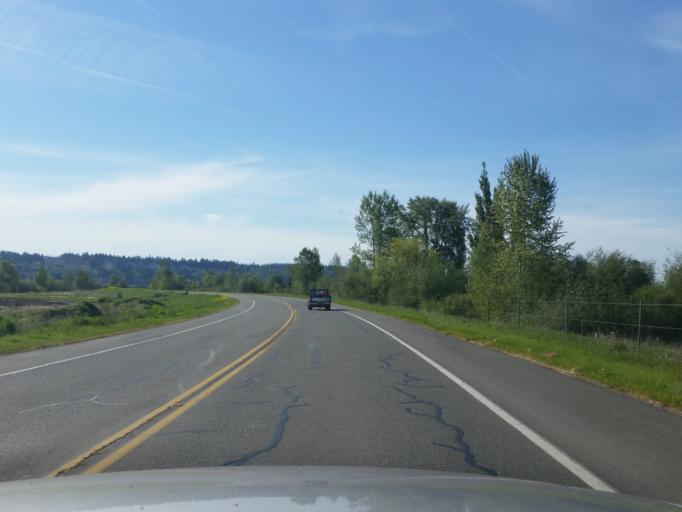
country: US
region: Washington
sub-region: Snohomish County
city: Fobes Hill
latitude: 47.9236
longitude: -122.1553
